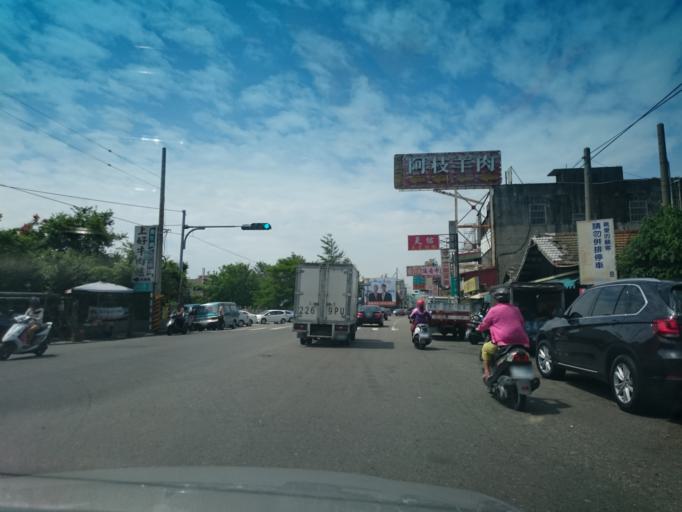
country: TW
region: Taiwan
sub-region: Changhua
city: Chang-hua
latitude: 23.9572
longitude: 120.4843
